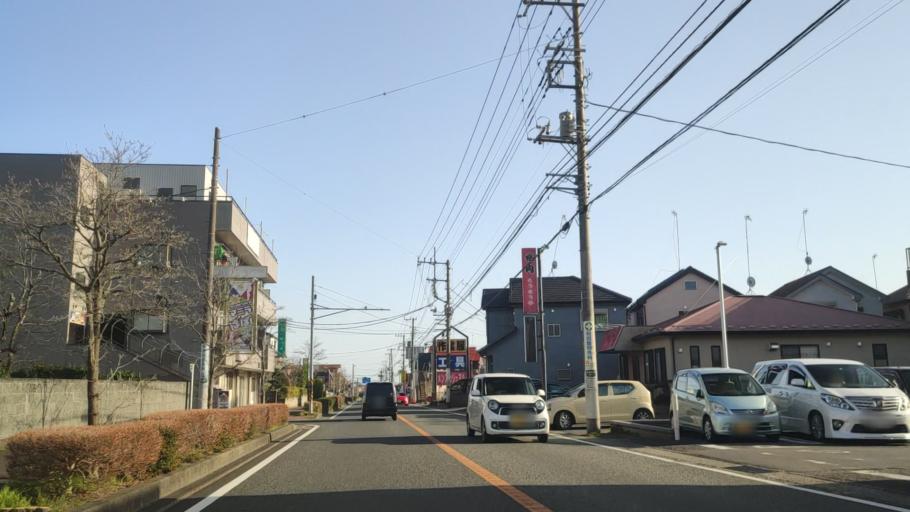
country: JP
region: Kanagawa
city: Zama
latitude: 35.5094
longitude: 139.3391
